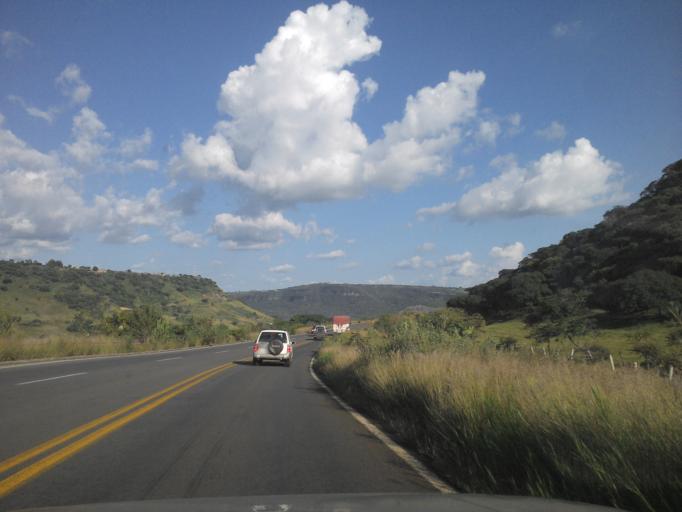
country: MX
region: Jalisco
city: Atotonilco el Alto
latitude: 20.5657
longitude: -102.5194
